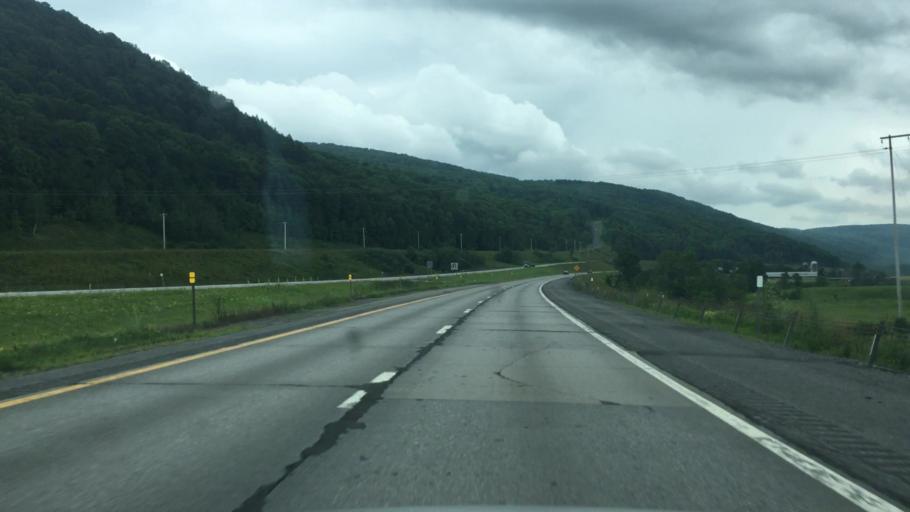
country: US
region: New York
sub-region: Otsego County
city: Worcester
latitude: 42.6256
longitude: -74.6620
